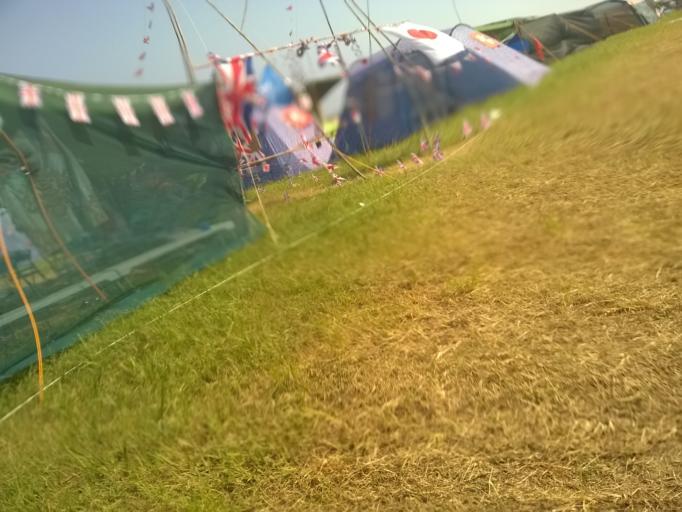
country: JP
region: Yamaguchi
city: Ogori-shimogo
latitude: 34.0121
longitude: 131.3780
